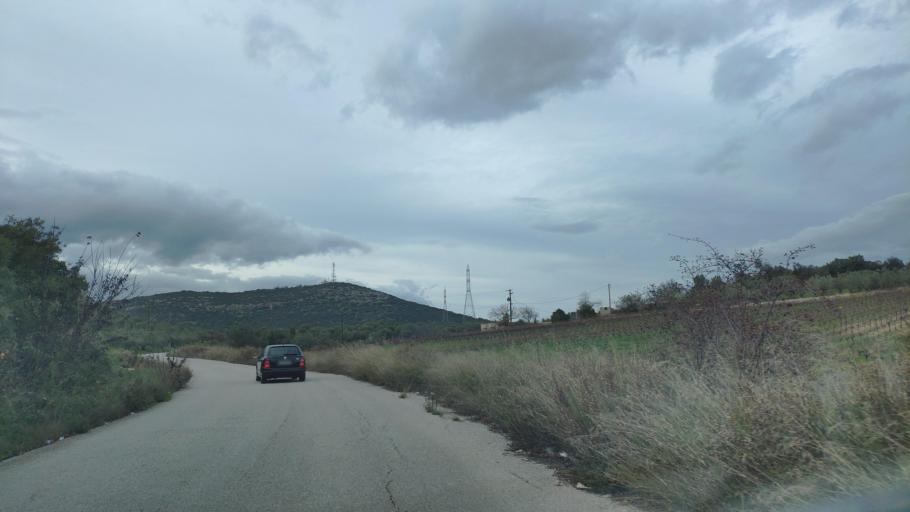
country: GR
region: Peloponnese
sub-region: Nomos Korinthias
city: Ayios Vasilios
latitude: 37.7937
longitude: 22.7306
